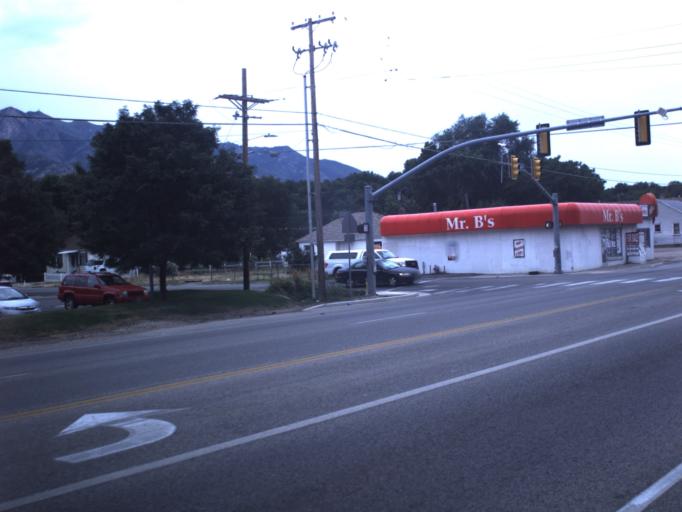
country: US
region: Utah
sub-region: Weber County
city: Ogden
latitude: 41.2522
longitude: -111.9781
